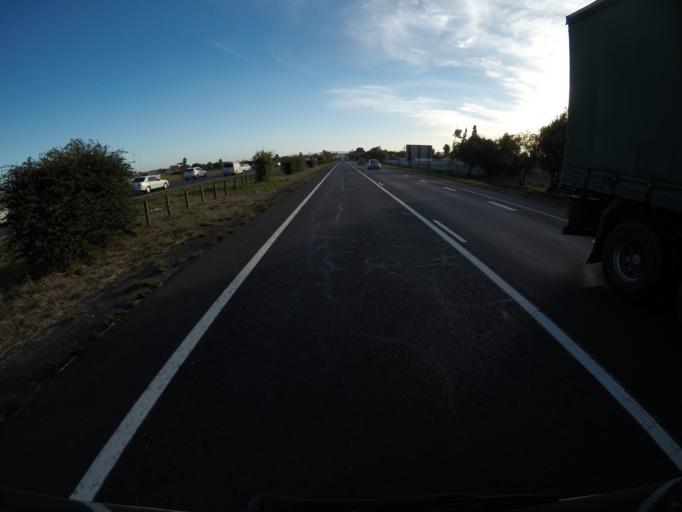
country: ZA
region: Western Cape
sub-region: City of Cape Town
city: Kraaifontein
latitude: -33.8473
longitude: 18.7119
